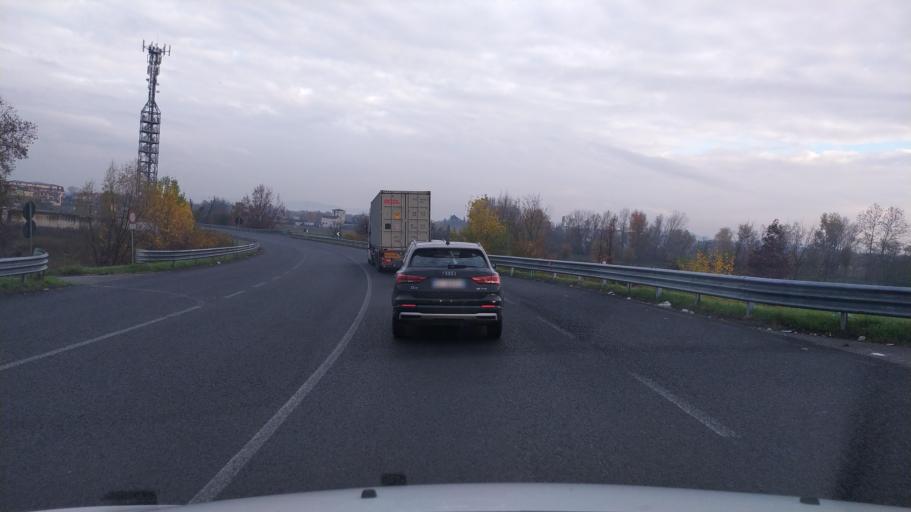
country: IT
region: Lombardy
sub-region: Provincia di Bergamo
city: Calcio
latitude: 45.5035
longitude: 9.8589
